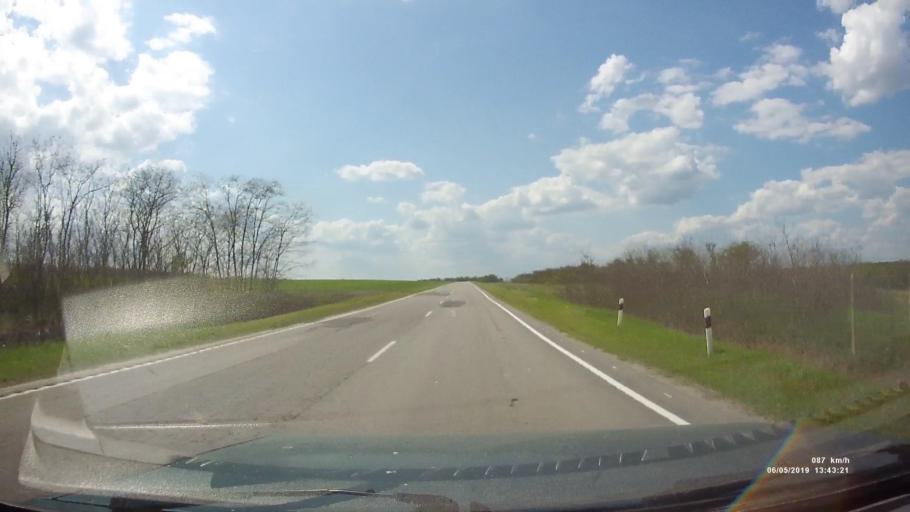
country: RU
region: Rostov
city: Semikarakorsk
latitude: 47.6603
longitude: 40.6401
